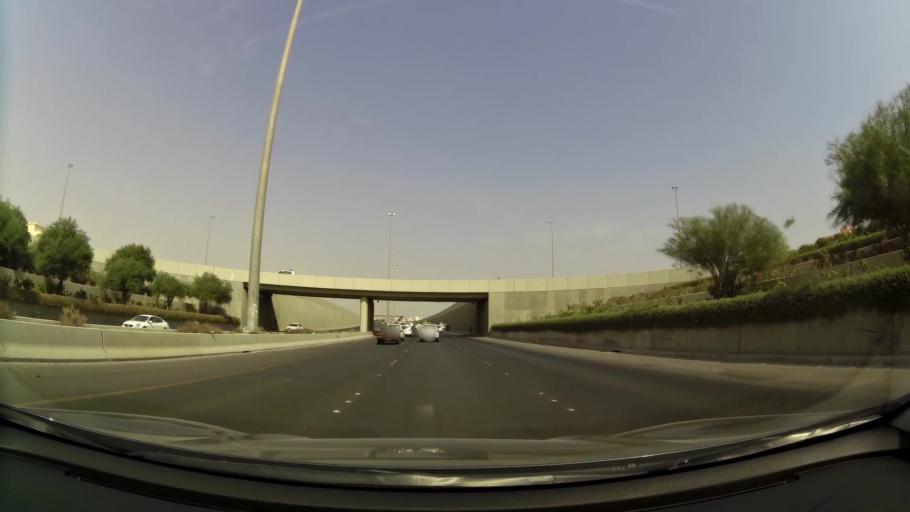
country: KW
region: Al Ahmadi
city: Al Manqaf
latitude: 29.1065
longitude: 48.1183
